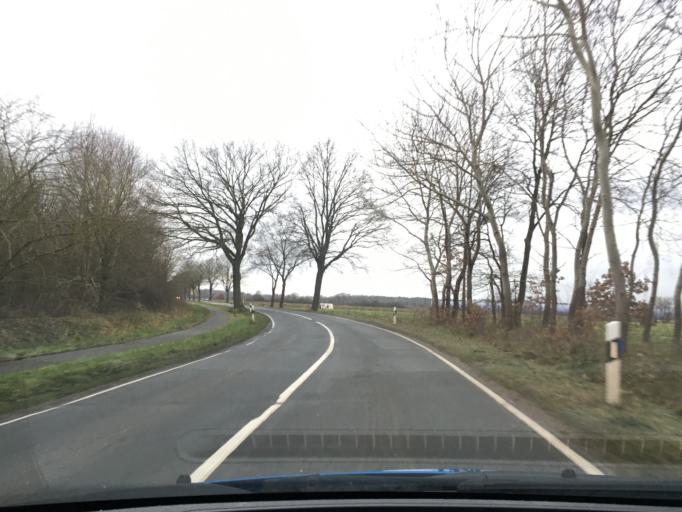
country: DE
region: Lower Saxony
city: Winsen
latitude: 53.3247
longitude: 10.2261
